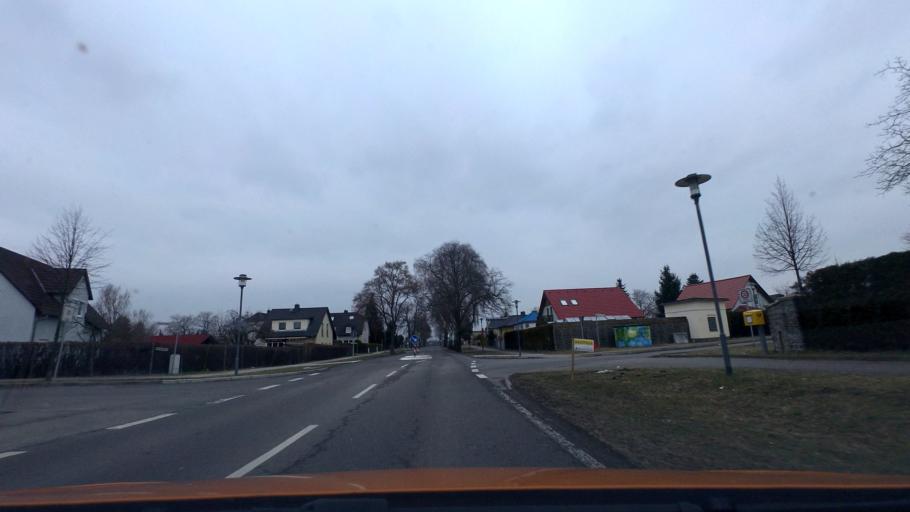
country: DE
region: Brandenburg
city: Ahrensfelde
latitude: 52.5680
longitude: 13.5904
